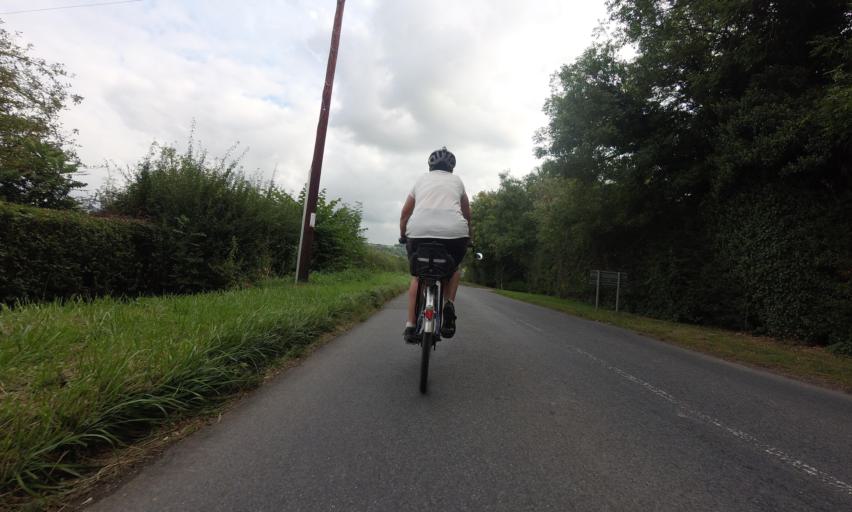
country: GB
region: England
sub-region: Gloucestershire
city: Winchcombe
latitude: 51.9786
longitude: -1.9966
